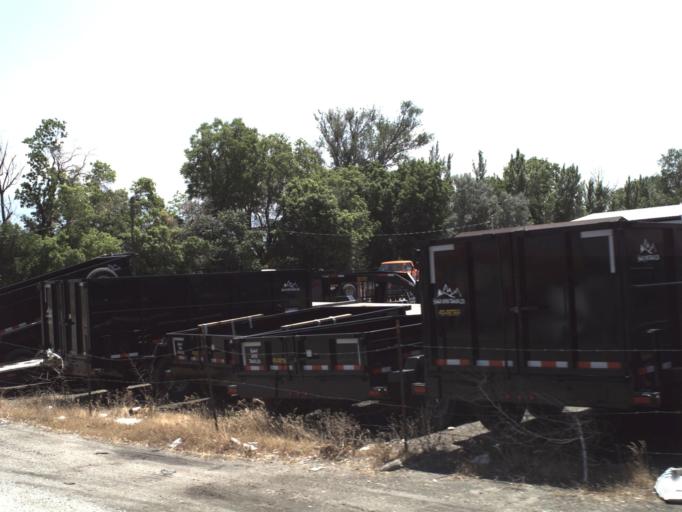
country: US
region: Utah
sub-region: Weber County
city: Marriott-Slaterville
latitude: 41.2447
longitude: -112.0230
